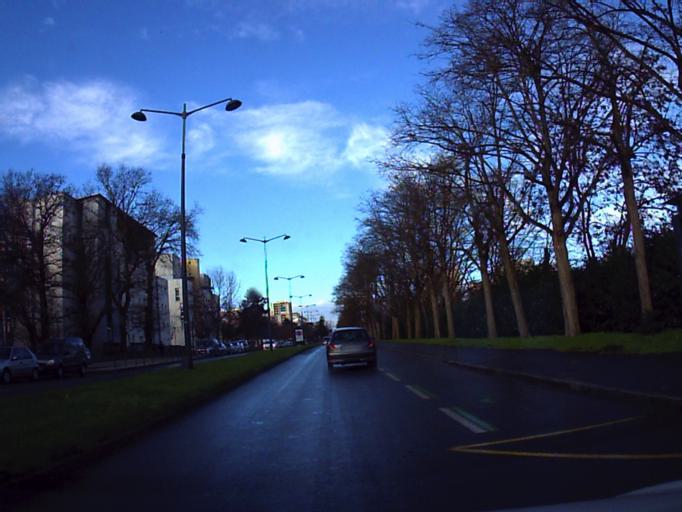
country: FR
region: Brittany
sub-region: Departement d'Ille-et-Vilaine
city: Rennes
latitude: 48.0829
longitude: -1.6824
